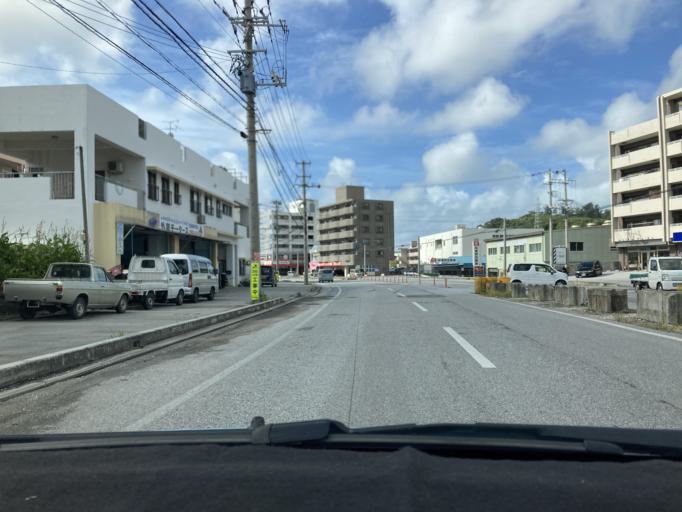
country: JP
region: Okinawa
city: Tomigusuku
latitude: 26.1885
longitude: 127.6882
